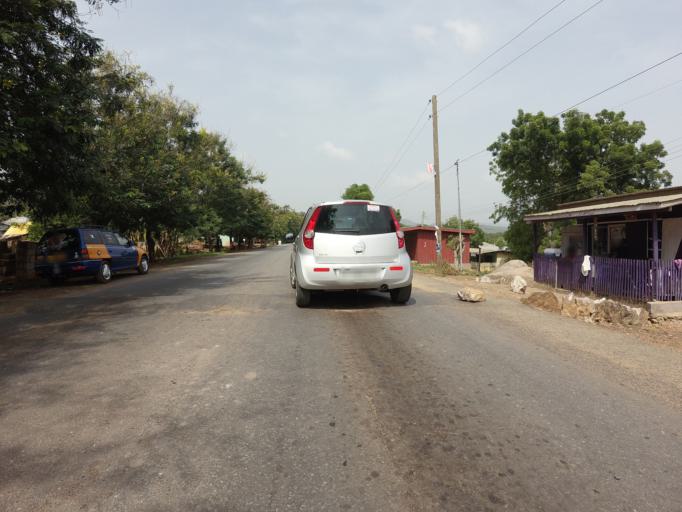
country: GH
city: Akropong
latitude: 6.2630
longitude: 0.0784
